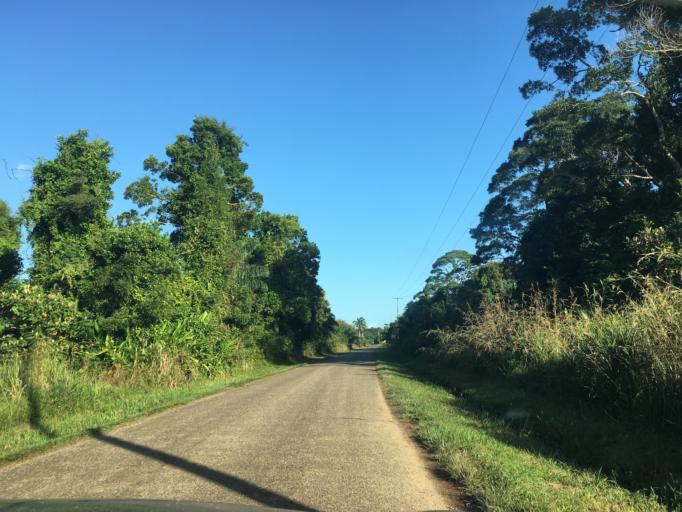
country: BZ
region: Stann Creek
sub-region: Dangriga
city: Dangriga
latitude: 16.8211
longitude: -88.3265
